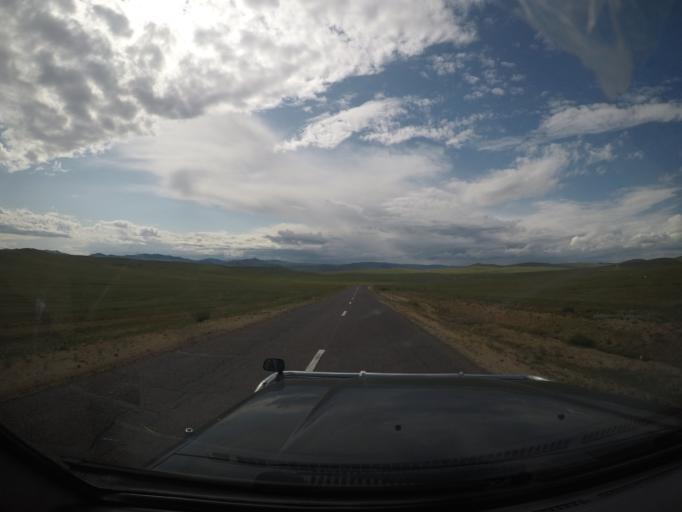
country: MN
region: Hentiy
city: Modot
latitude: 47.5913
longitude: 109.2621
